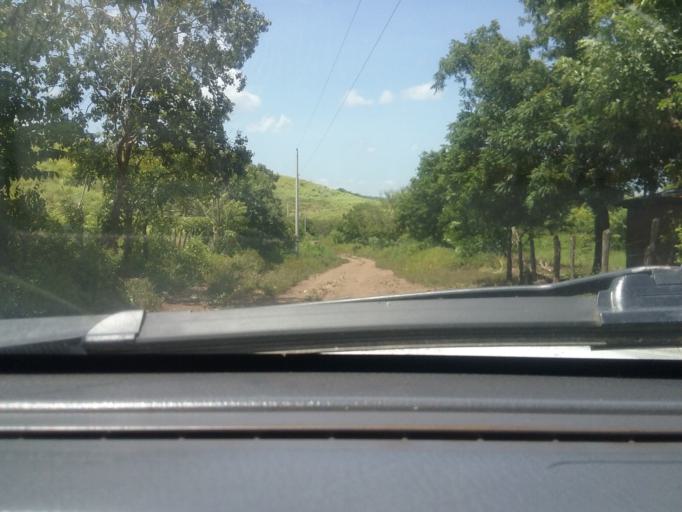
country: NI
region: Matagalpa
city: Terrabona
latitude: 12.6764
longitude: -85.9778
